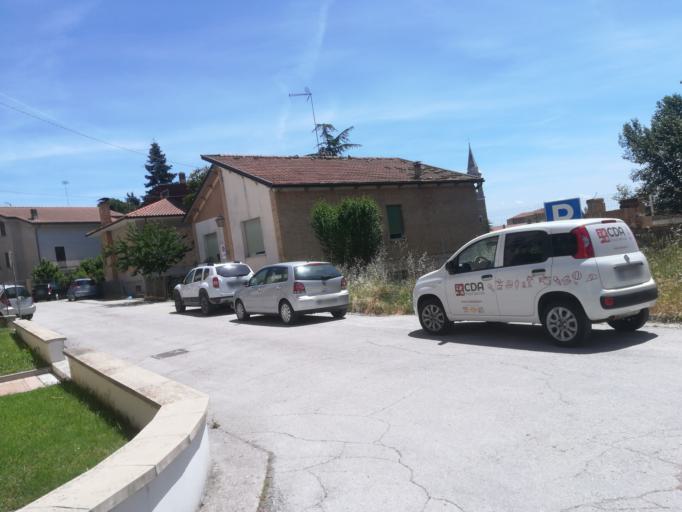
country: IT
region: The Marches
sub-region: Provincia di Macerata
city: Mogliano
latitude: 43.1854
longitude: 13.4729
